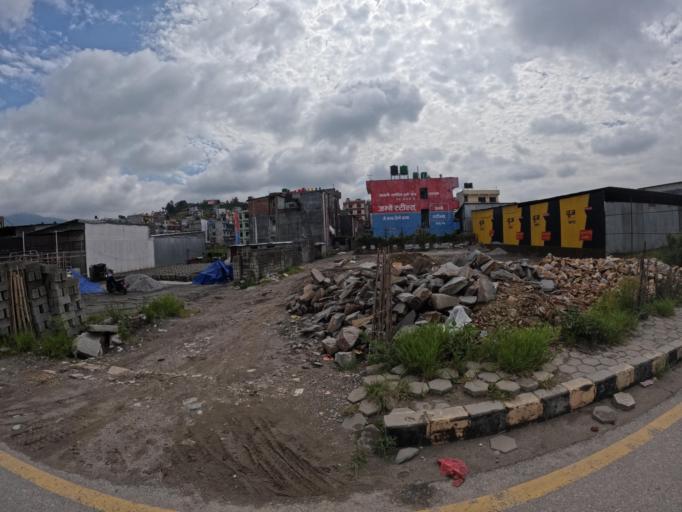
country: NP
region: Central Region
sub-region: Bagmati Zone
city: Kathmandu
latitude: 27.7591
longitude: 85.3162
